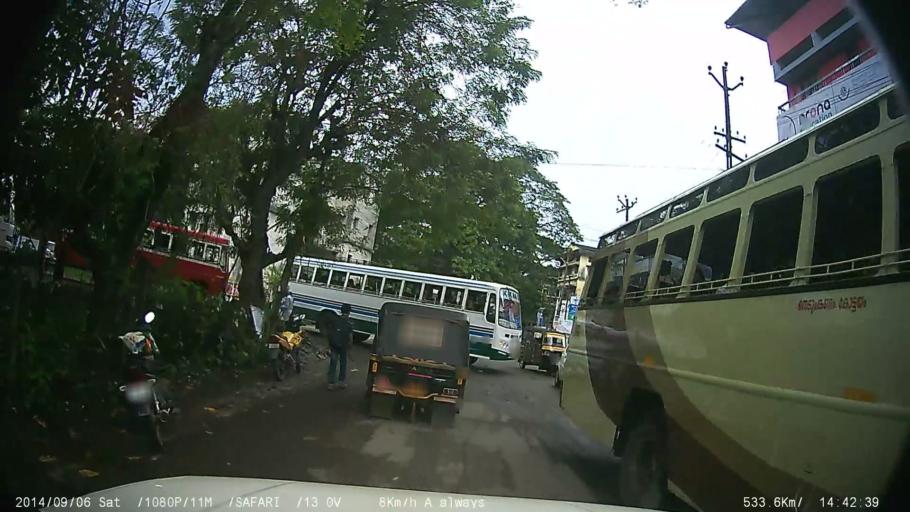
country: IN
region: Kerala
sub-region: Kottayam
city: Kottayam
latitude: 9.5951
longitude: 76.5291
